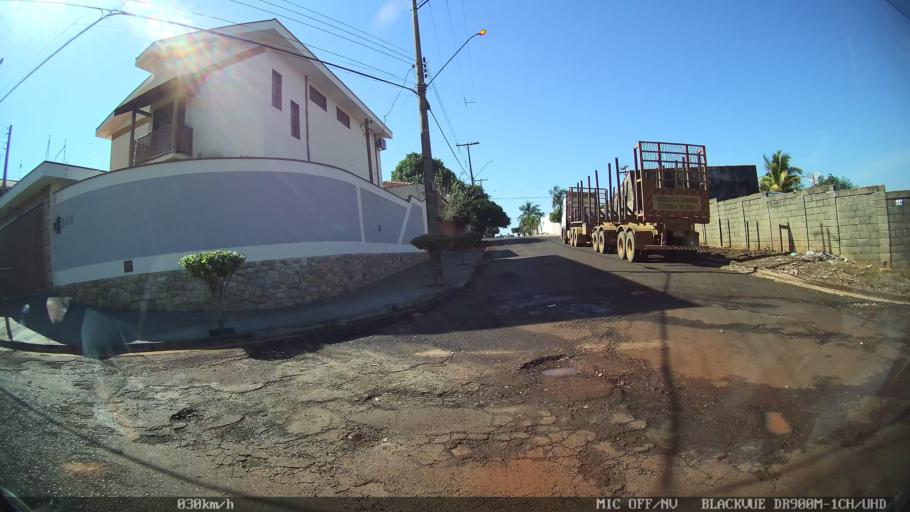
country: BR
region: Sao Paulo
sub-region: Batatais
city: Batatais
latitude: -20.8901
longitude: -47.5761
